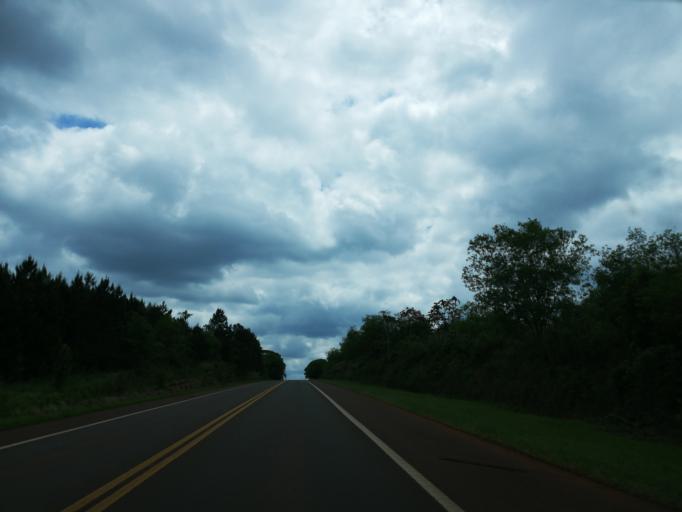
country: AR
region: Misiones
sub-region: Departamento de Leandro N. Alem
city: Leandro N. Alem
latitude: -27.6471
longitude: -55.3610
